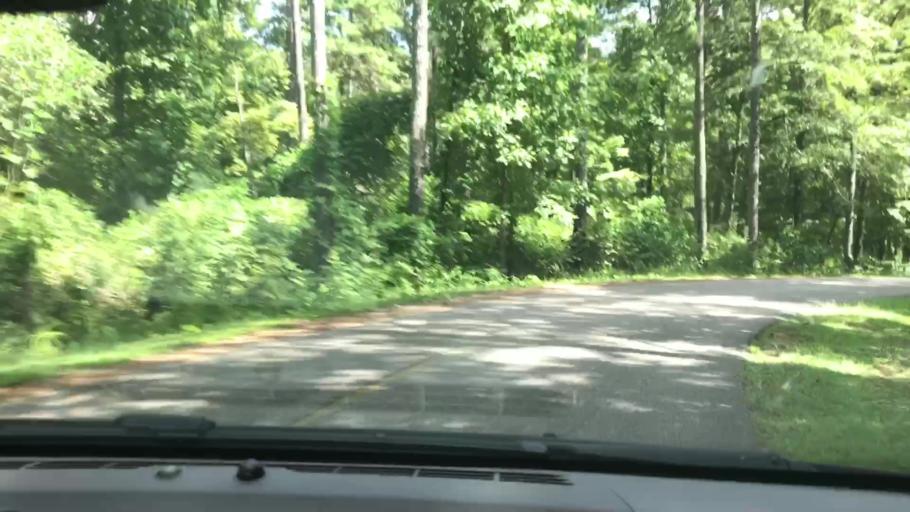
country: US
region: Georgia
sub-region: Troup County
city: La Grange
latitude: 33.1041
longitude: -85.1275
